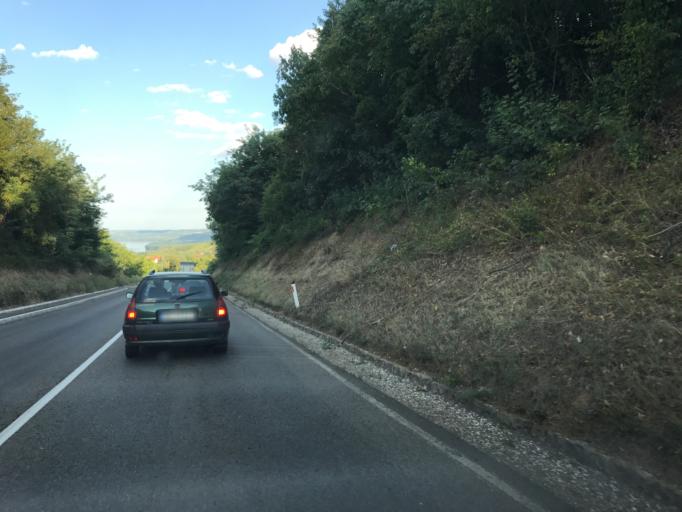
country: RS
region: Central Serbia
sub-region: Belgrade
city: Grocka
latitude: 44.6950
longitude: 20.6751
